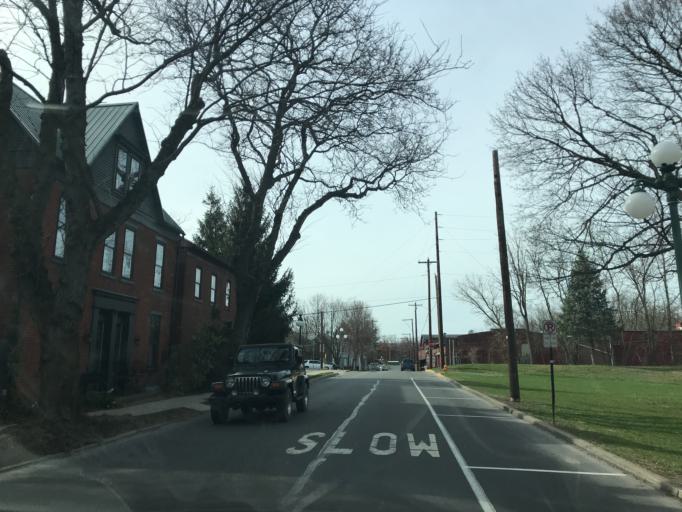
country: US
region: Pennsylvania
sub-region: Union County
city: Lewisburg
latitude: 40.9671
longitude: -76.8822
